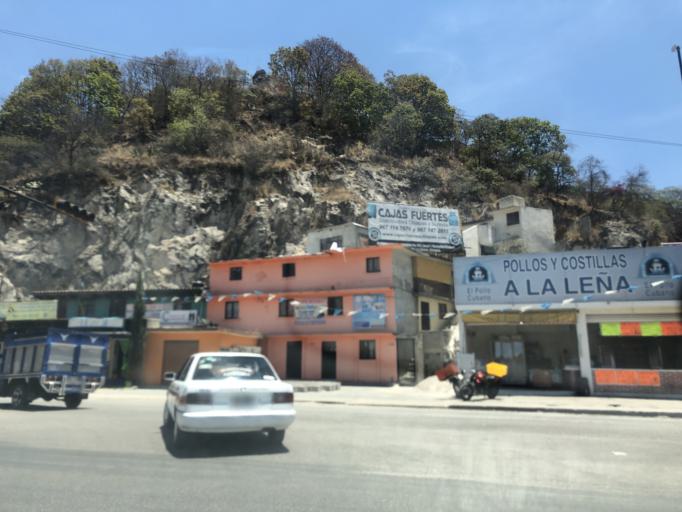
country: MX
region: Chiapas
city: San Cristobal de las Casas
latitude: 16.7214
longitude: -92.6340
